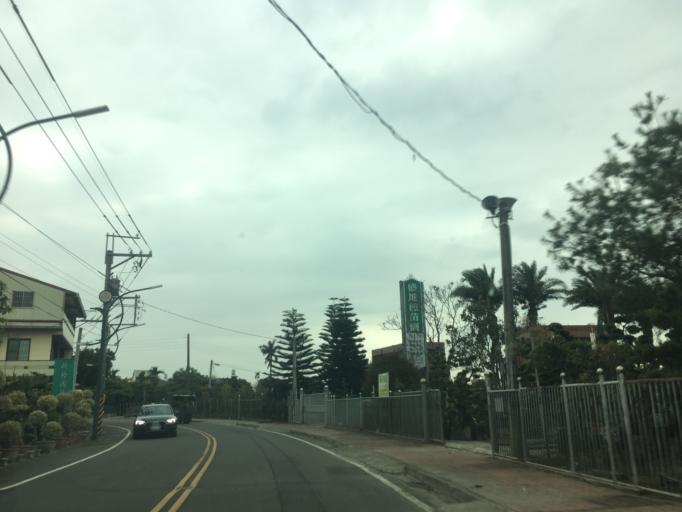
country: TW
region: Taiwan
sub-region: Nantou
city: Nantou
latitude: 23.9035
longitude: 120.5332
